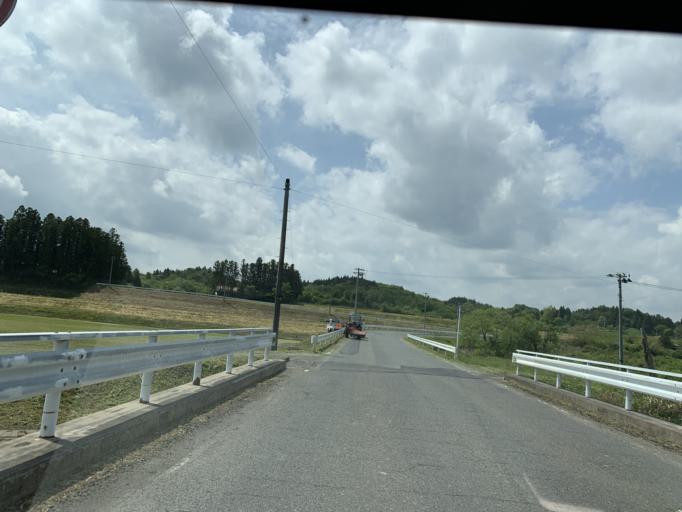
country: JP
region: Miyagi
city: Furukawa
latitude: 38.7684
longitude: 140.9533
